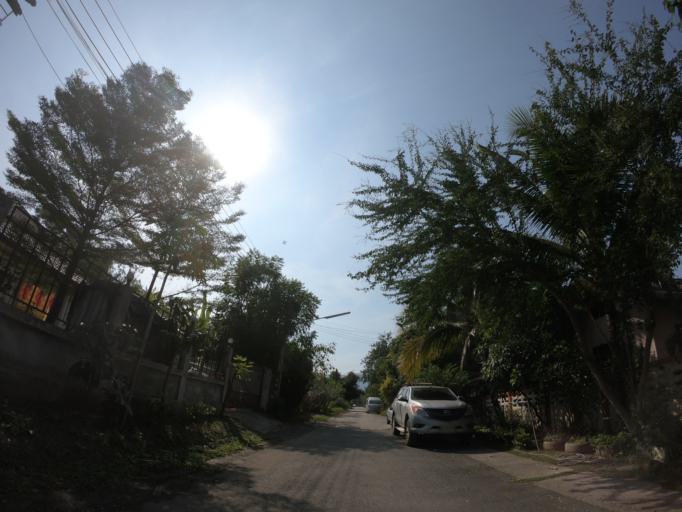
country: TH
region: Chiang Mai
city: Chiang Mai
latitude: 18.8225
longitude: 98.9885
